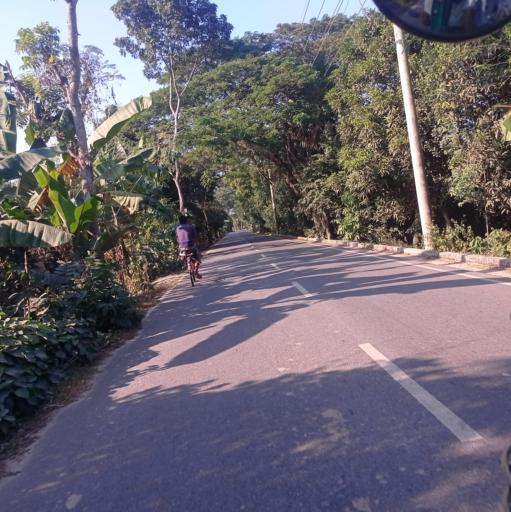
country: BD
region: Dhaka
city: Bajitpur
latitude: 24.1441
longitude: 90.8158
